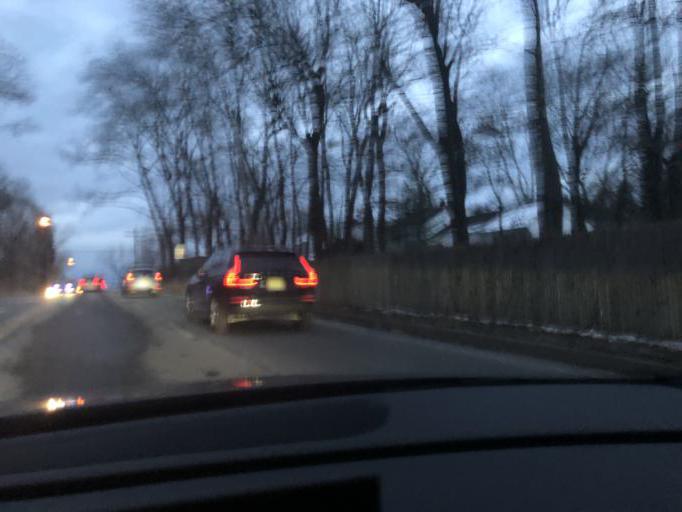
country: US
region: New Jersey
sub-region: Morris County
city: Morristown
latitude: 40.7947
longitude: -74.4473
